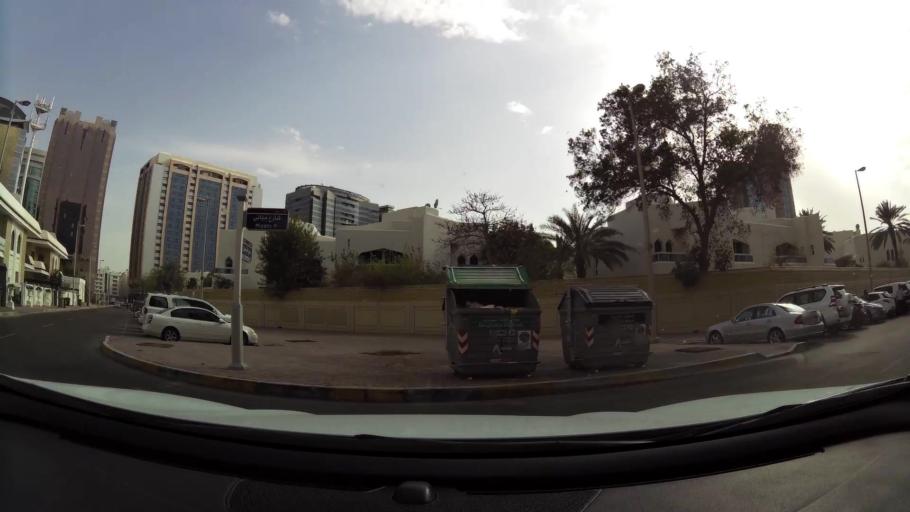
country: AE
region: Abu Dhabi
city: Abu Dhabi
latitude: 24.4751
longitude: 54.3455
